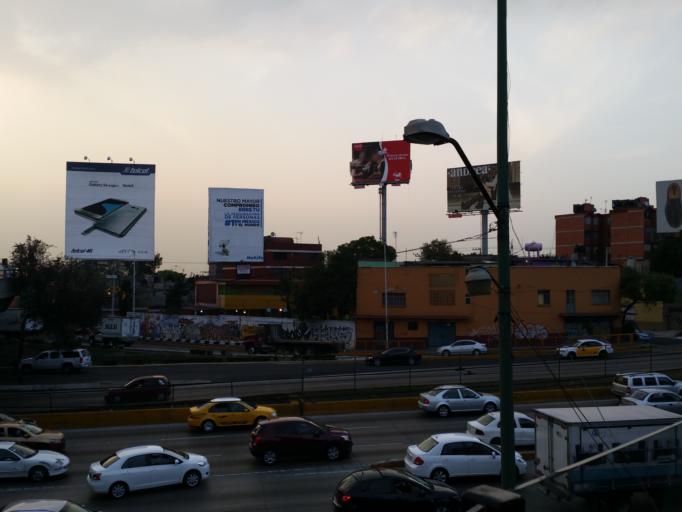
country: MX
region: Mexico City
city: Venustiano Carranza
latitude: 19.4355
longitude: -99.0865
